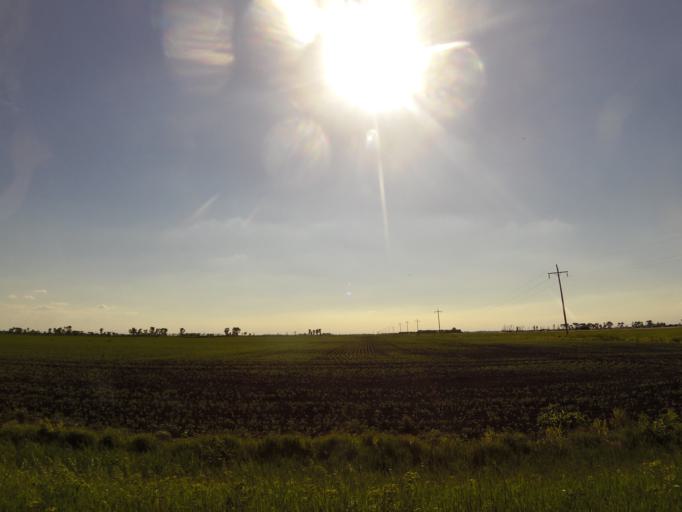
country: US
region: North Dakota
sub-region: Walsh County
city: Grafton
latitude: 48.4114
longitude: -97.2339
